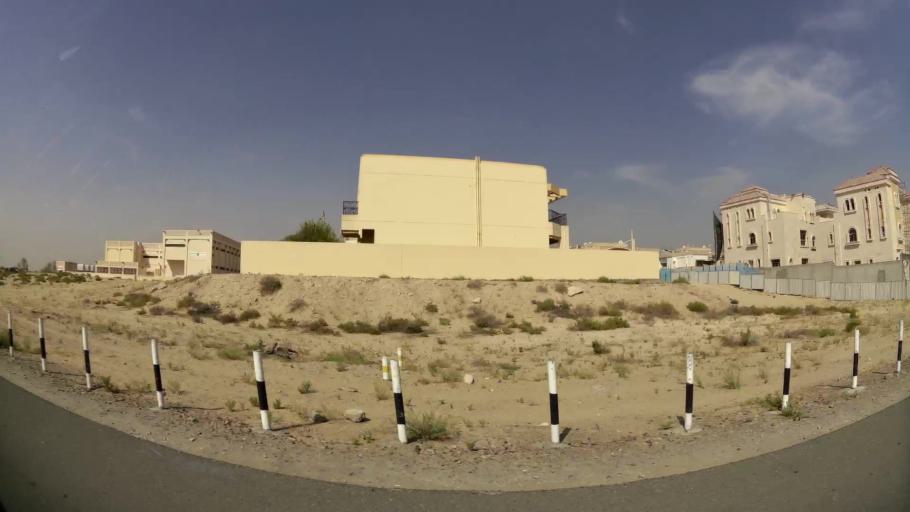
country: AE
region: Ash Shariqah
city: Sharjah
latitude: 25.2173
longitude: 55.4268
